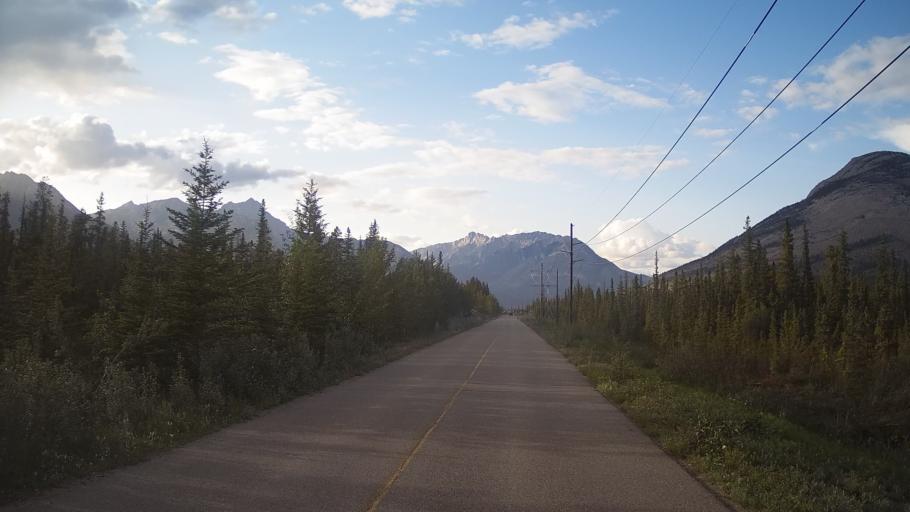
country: CA
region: Alberta
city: Jasper Park Lodge
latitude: 53.0054
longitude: -118.0855
